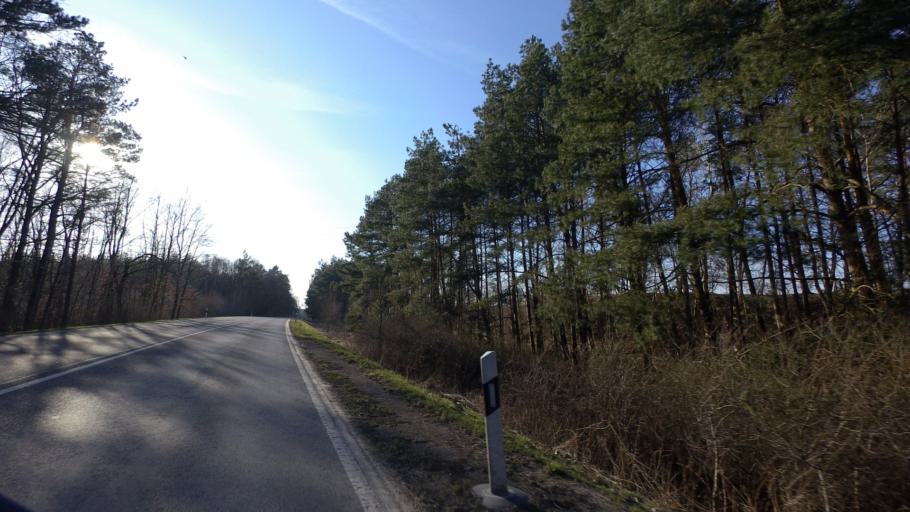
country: DE
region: Brandenburg
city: Althuttendorf
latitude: 52.9510
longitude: 13.8203
